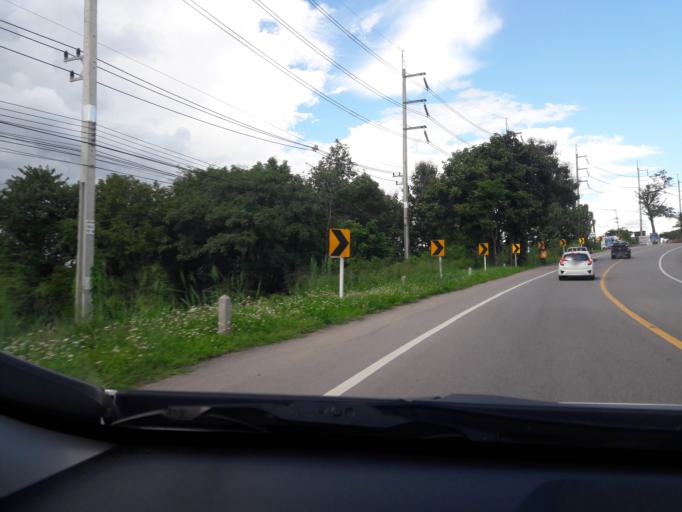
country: TH
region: Mae Hong Son
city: Mae Hi
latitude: 19.3363
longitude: 98.4317
